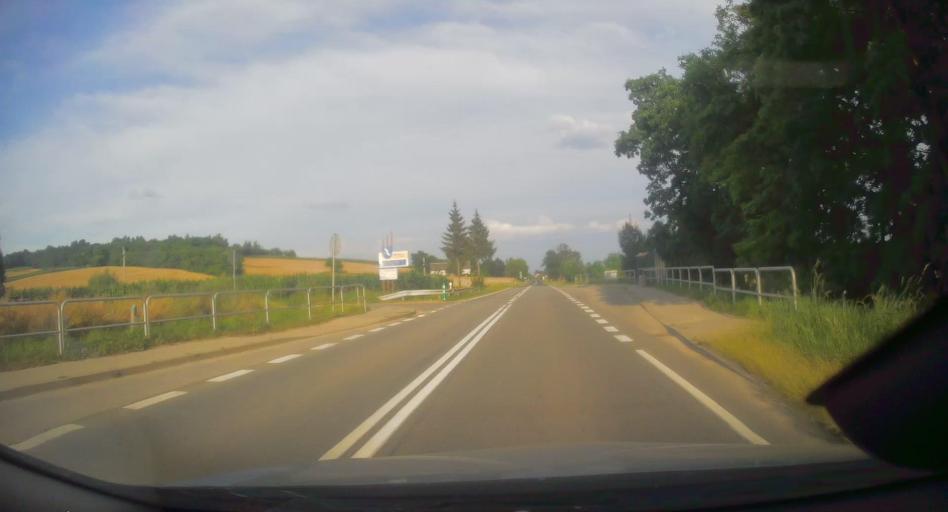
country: PL
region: Lesser Poland Voivodeship
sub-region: Powiat bochenski
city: Dziewin
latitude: 50.1432
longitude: 20.4801
